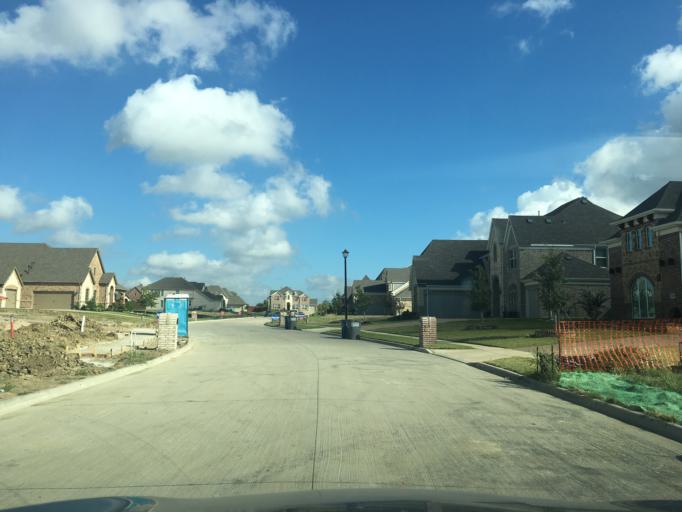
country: US
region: Texas
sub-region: Dallas County
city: Sachse
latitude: 32.9690
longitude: -96.5750
